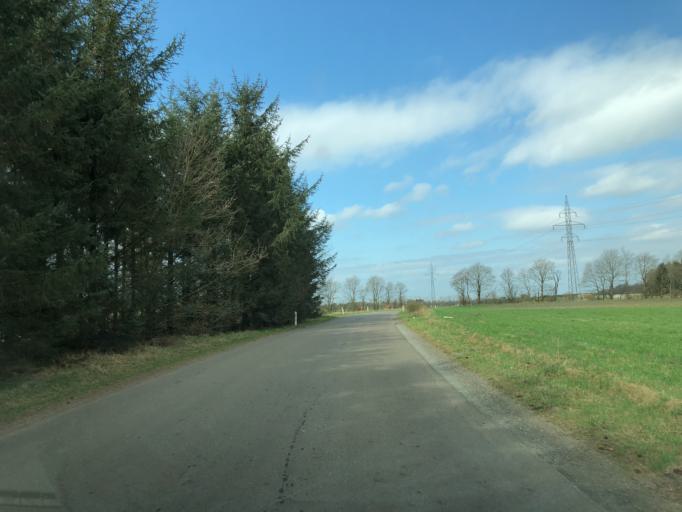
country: DK
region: South Denmark
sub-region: Vejle Kommune
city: Give
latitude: 55.9156
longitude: 9.2191
